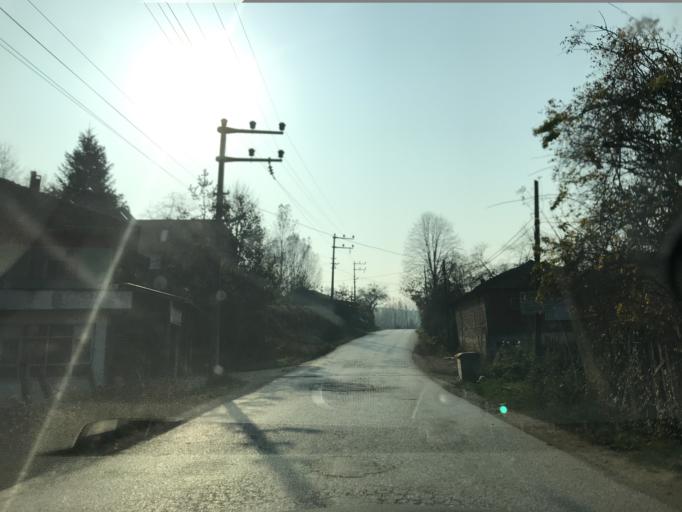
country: TR
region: Duzce
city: Cumayeri
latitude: 40.9070
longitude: 30.9506
